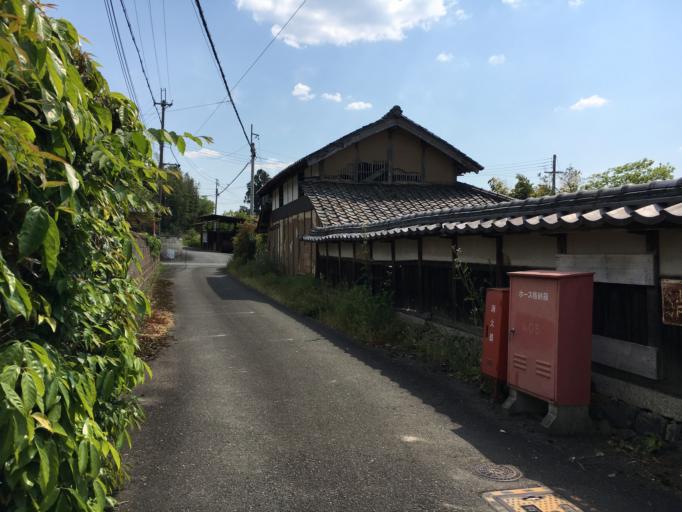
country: JP
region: Kyoto
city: Kameoka
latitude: 35.0847
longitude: 135.5559
